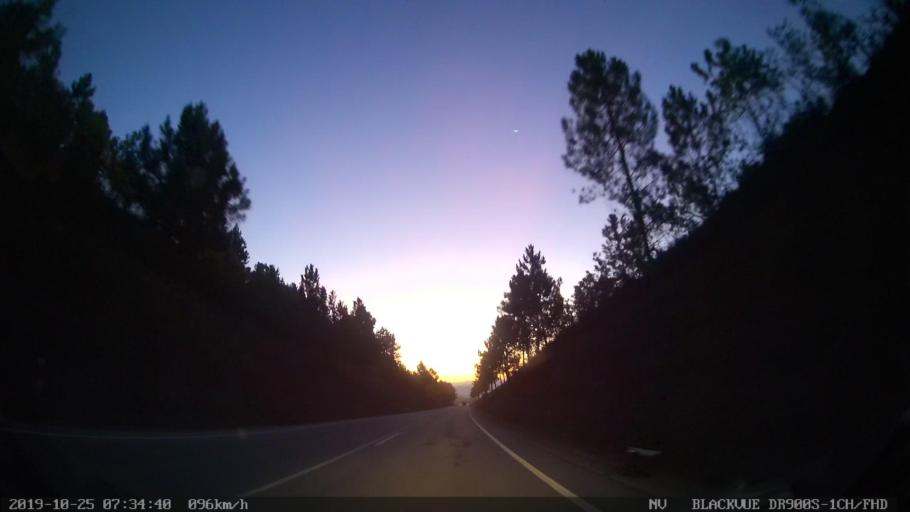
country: PT
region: Vila Real
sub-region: Sabrosa
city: Sabrosa
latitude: 41.2612
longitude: -7.6099
